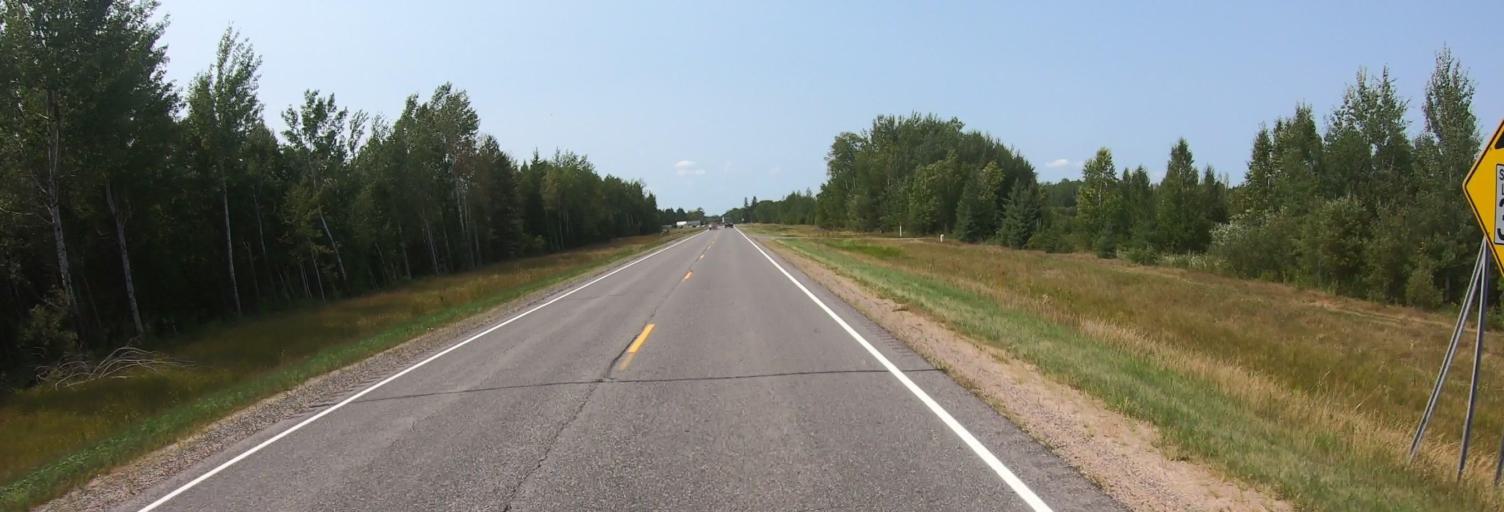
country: US
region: Minnesota
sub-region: Koochiching County
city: International Falls
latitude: 48.5126
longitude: -93.7883
